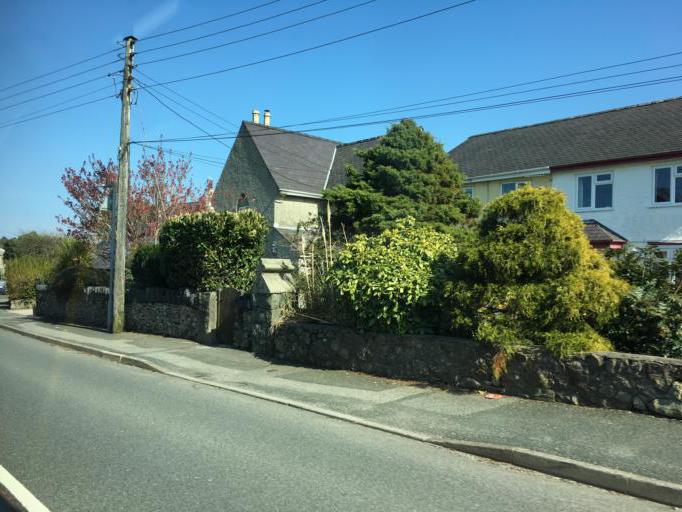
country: GB
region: Wales
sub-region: Anglesey
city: Menai Bridge
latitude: 53.2061
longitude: -4.1714
